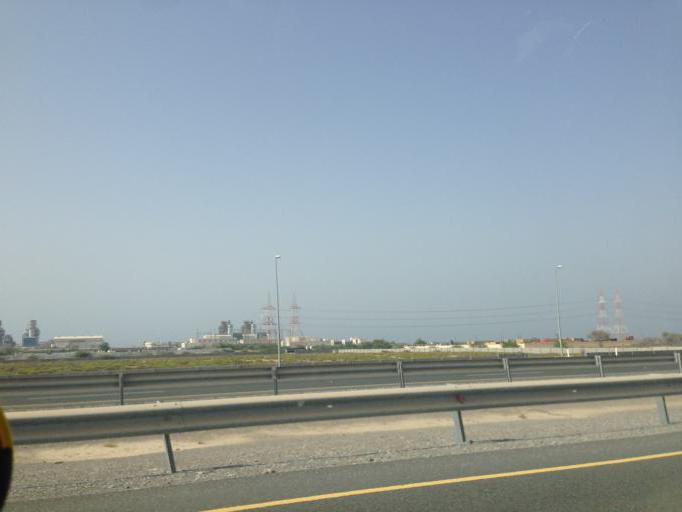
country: OM
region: Al Batinah
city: Barka'
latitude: 23.6991
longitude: 57.9830
